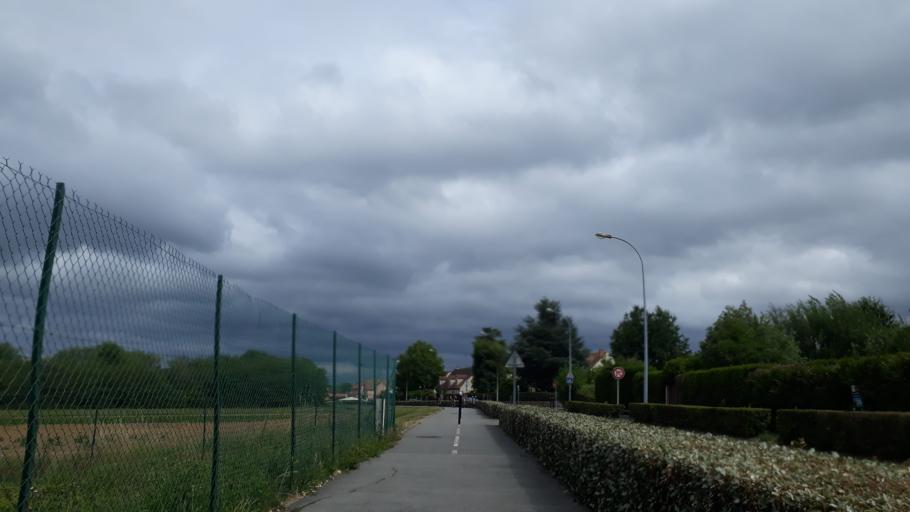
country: FR
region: Ile-de-France
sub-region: Departement de l'Essonne
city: Nozay
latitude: 48.6627
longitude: 2.2378
